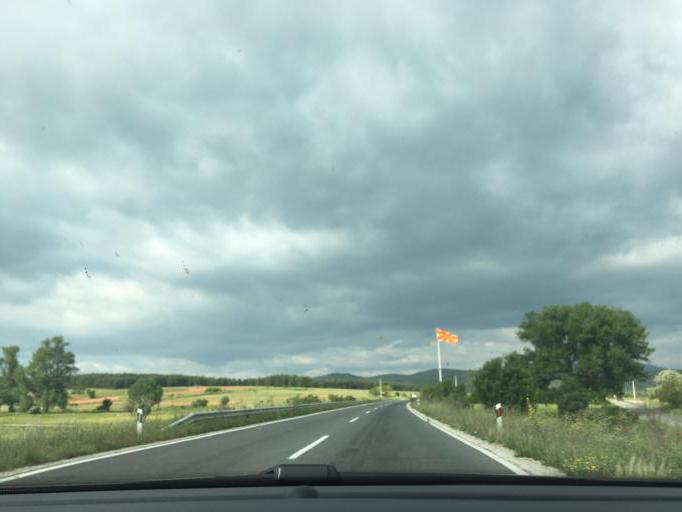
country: MK
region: Prilep
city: Topolcani
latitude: 41.2674
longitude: 21.4735
